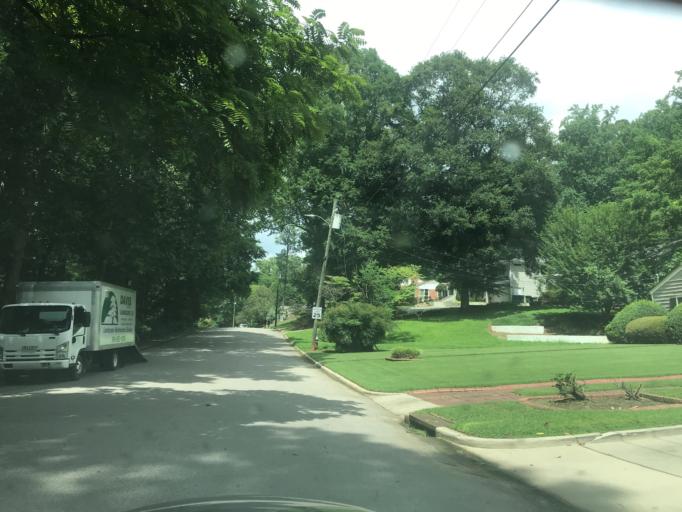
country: US
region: North Carolina
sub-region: Wake County
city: West Raleigh
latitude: 35.8143
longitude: -78.6374
